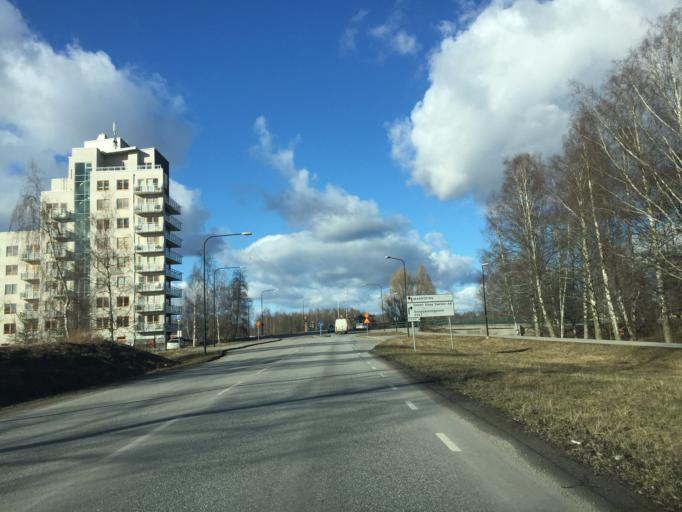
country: SE
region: OErebro
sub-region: Orebro Kommun
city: Orebro
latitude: 59.2715
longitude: 15.2415
